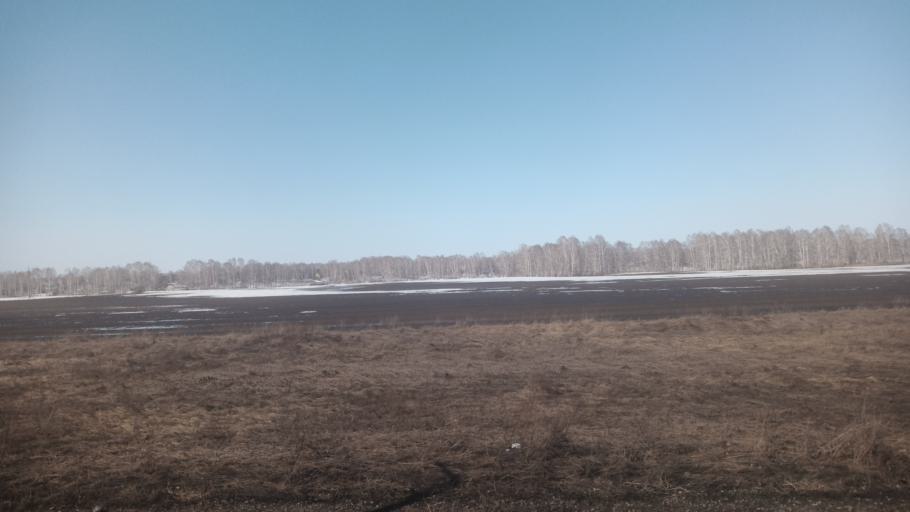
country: RU
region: Altai Krai
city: Logovskoye
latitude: 53.4806
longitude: 84.1303
